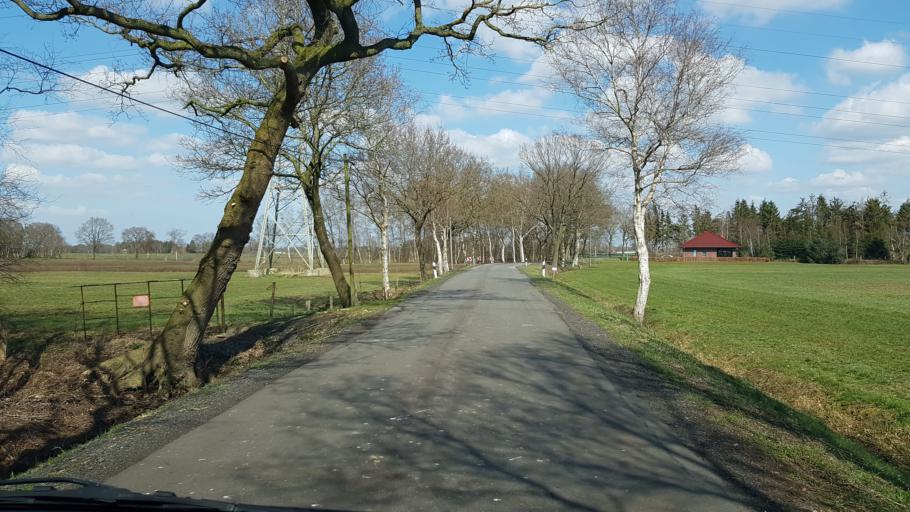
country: DE
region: Lower Saxony
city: Rastede
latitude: 53.2969
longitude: 8.1969
